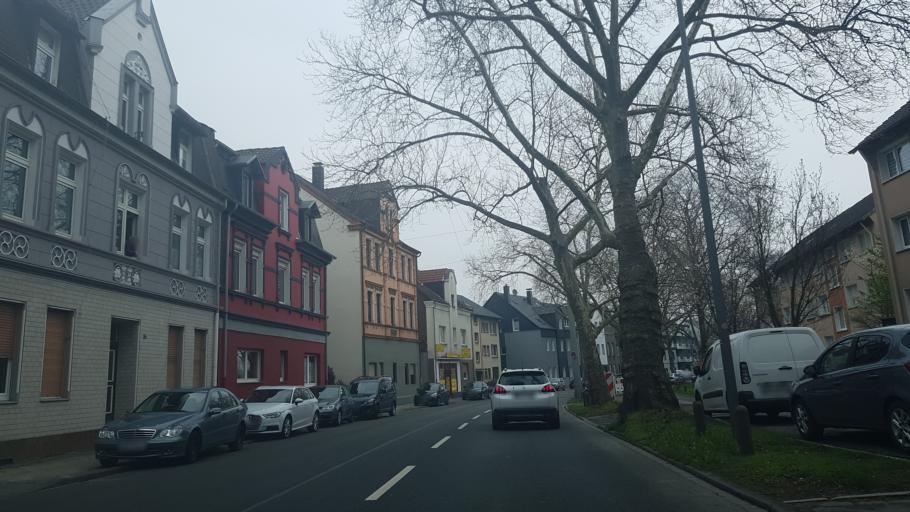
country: DE
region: North Rhine-Westphalia
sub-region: Regierungsbezirk Munster
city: Gelsenkirchen
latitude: 51.4866
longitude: 7.1352
